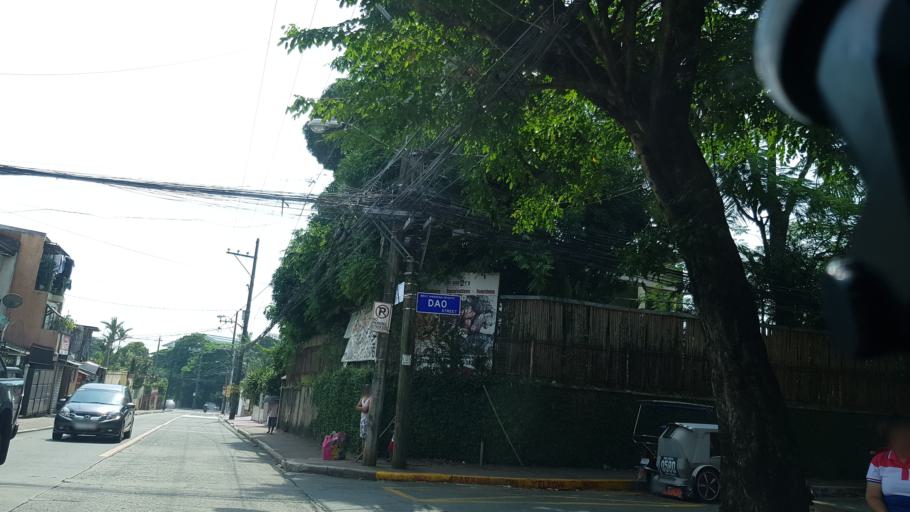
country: PH
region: Calabarzon
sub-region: Province of Rizal
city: Antipolo
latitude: 14.6541
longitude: 121.1198
